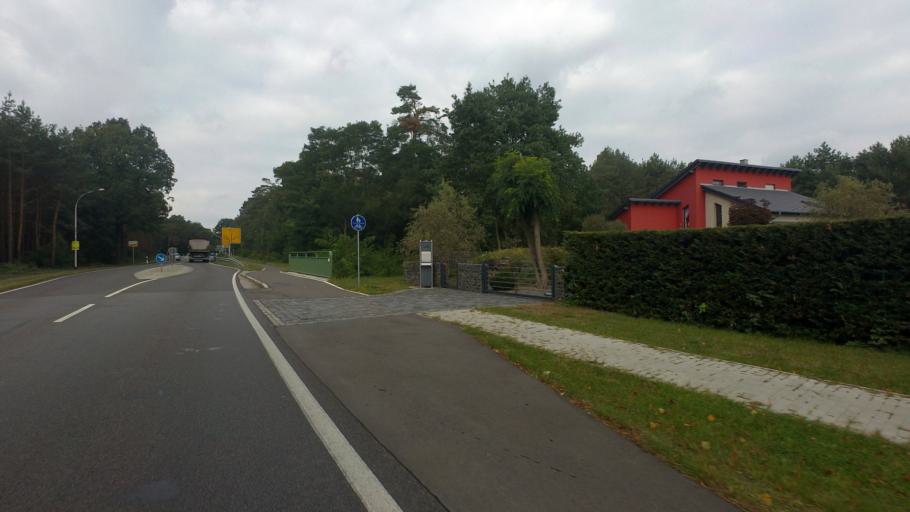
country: DE
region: Brandenburg
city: Bad Liebenwerda
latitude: 51.5508
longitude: 13.3811
